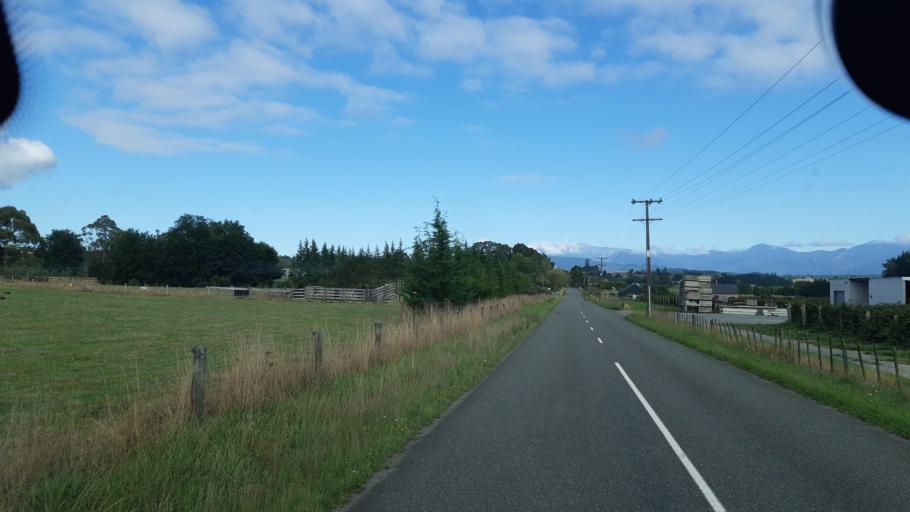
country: NZ
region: Tasman
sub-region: Tasman District
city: Mapua
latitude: -41.2412
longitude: 173.0322
